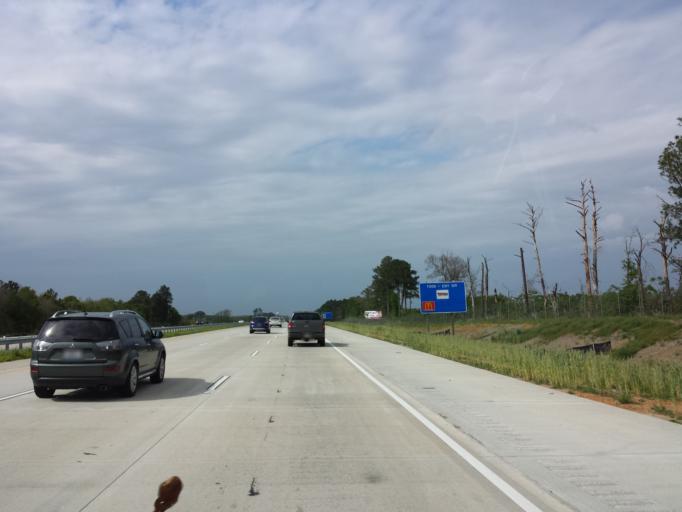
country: US
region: Georgia
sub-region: Dooly County
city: Vienna
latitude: 32.0651
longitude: -83.7633
